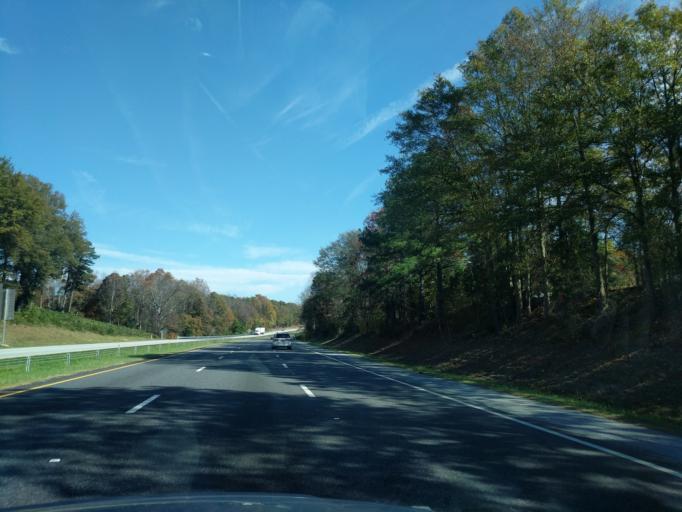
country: US
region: South Carolina
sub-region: Cherokee County
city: Blacksburg
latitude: 35.1648
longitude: -81.4506
